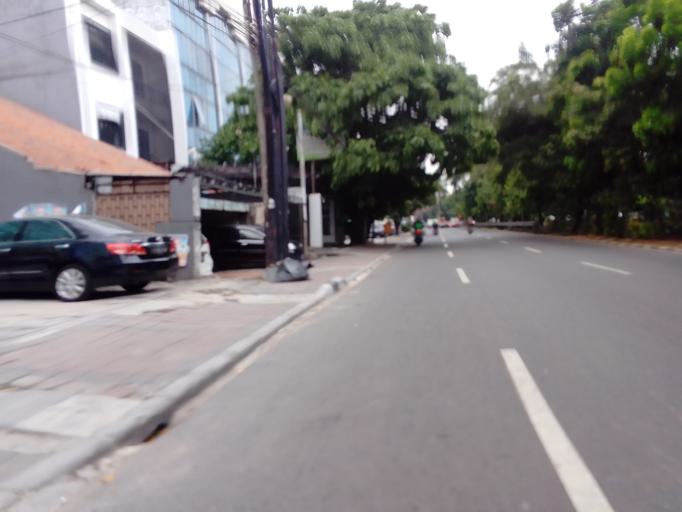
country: ID
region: Jakarta Raya
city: Jakarta
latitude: -6.1640
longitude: 106.8108
